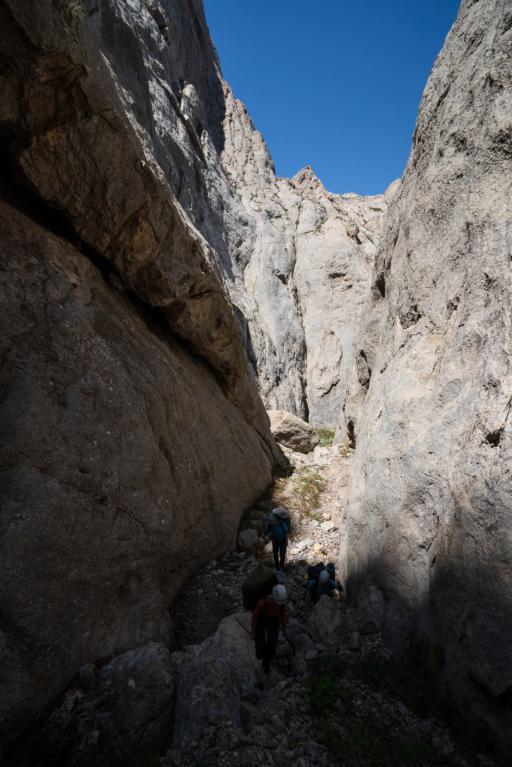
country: KZ
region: Ongtustik Qazaqstan
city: Ashchysay
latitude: 43.7689
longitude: 68.7948
